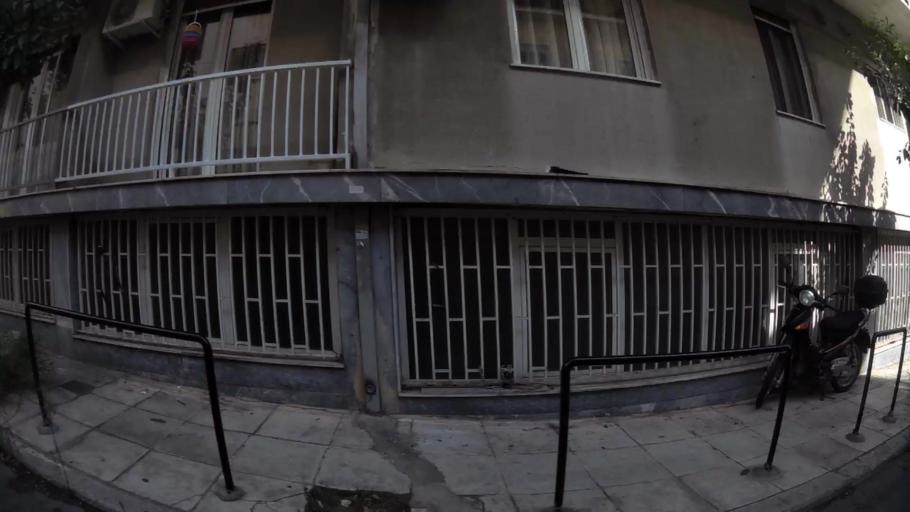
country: GR
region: Attica
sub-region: Nomos Piraios
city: Nikaia
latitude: 37.9613
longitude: 23.6472
